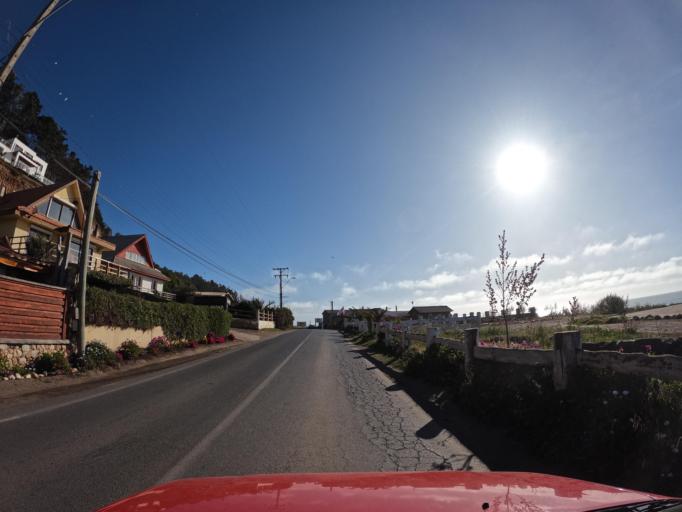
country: CL
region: Maule
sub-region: Provincia de Talca
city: Constitucion
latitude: -34.8874
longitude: -72.1707
